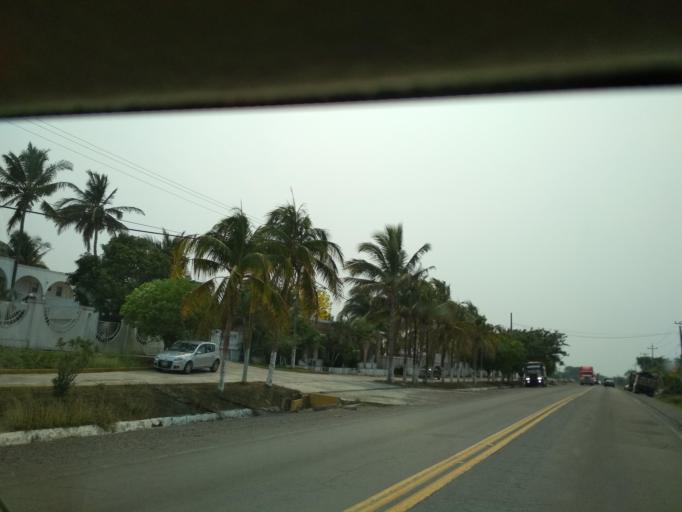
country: MX
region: Veracruz
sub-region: Veracruz
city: Delfino Victoria (Santa Fe)
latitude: 19.1939
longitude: -96.2879
